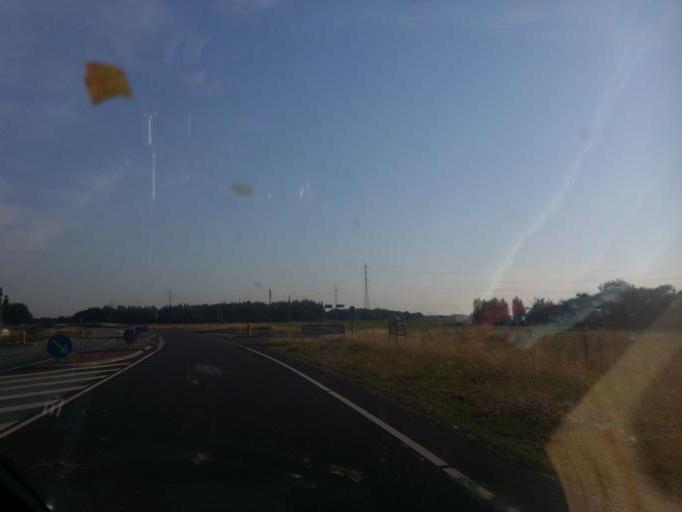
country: DK
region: South Denmark
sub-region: Tonder Kommune
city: Sherrebek
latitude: 55.0548
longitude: 8.8324
